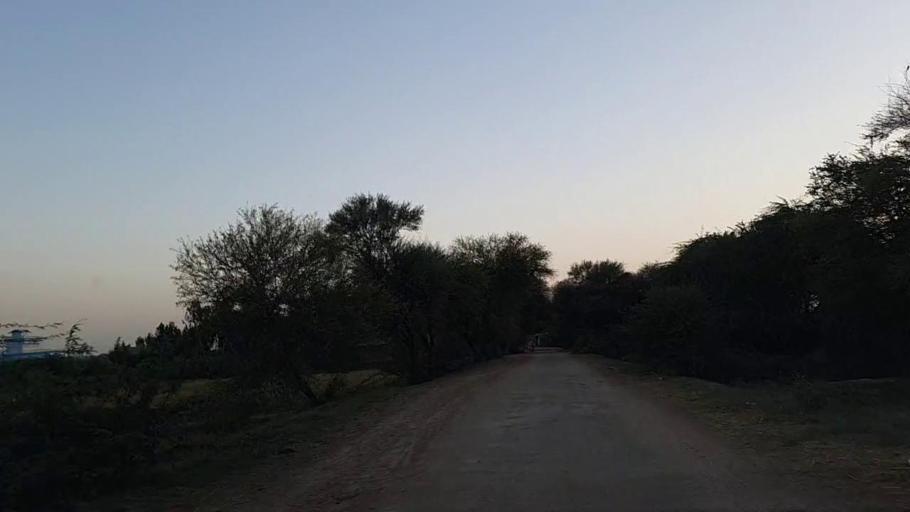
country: PK
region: Sindh
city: Mirpur Batoro
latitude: 24.6140
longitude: 68.1843
